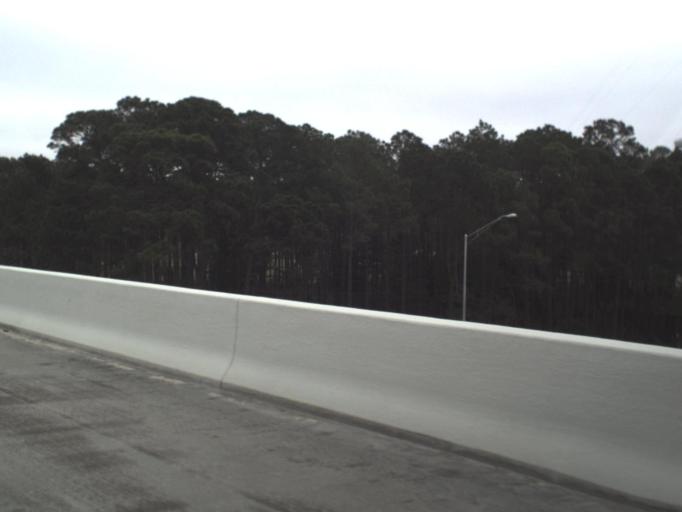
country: US
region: Florida
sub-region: Bay County
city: Upper Grand Lagoon
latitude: 30.1884
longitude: -85.7614
